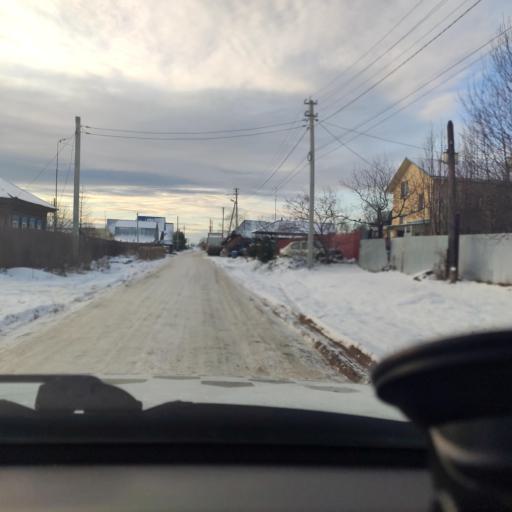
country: RU
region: Perm
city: Ferma
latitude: 57.9386
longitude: 56.3468
